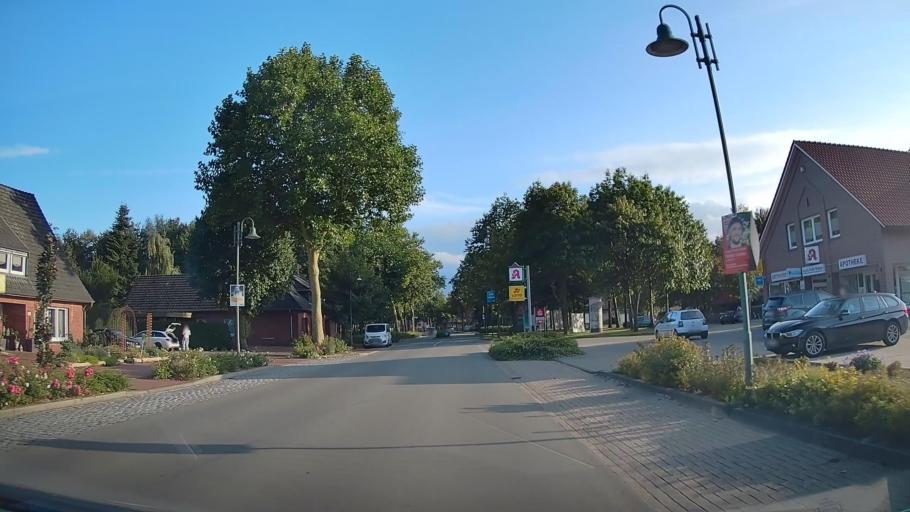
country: DE
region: Lower Saxony
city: Hilkenbrook
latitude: 53.0450
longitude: 7.7373
